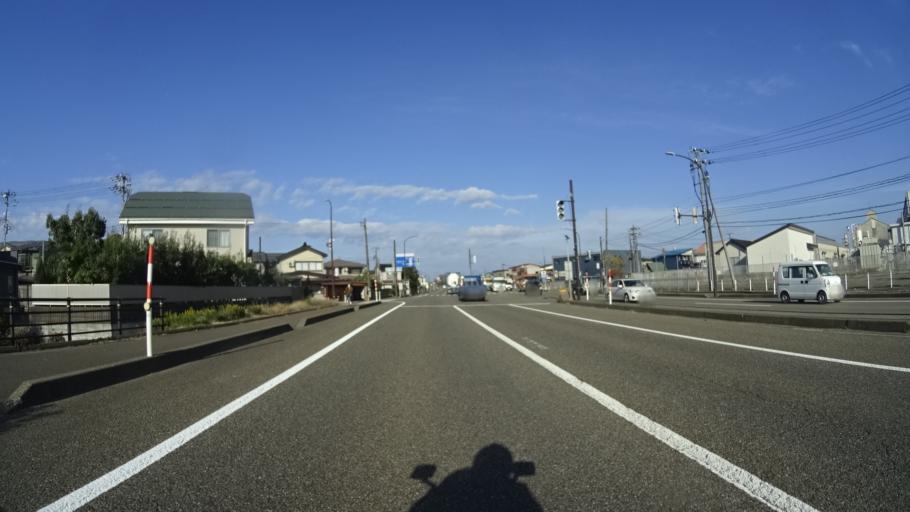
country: JP
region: Niigata
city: Joetsu
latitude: 37.1762
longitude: 138.2669
